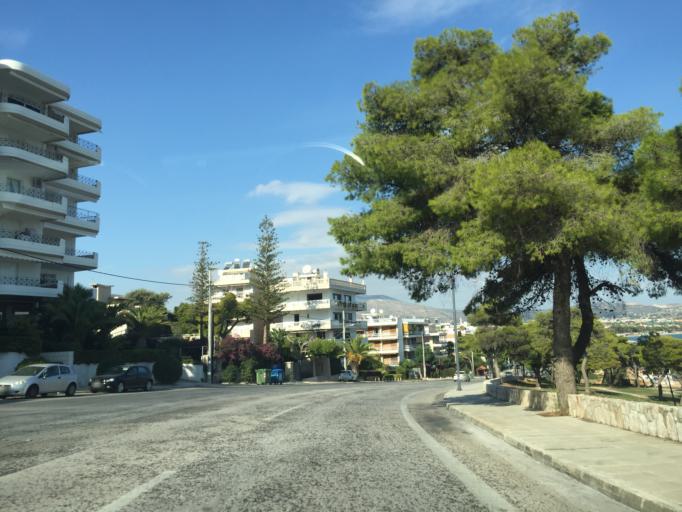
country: GR
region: Attica
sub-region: Nomarchia Anatolikis Attikis
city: Vouliagmeni
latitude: 37.8107
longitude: 23.7997
